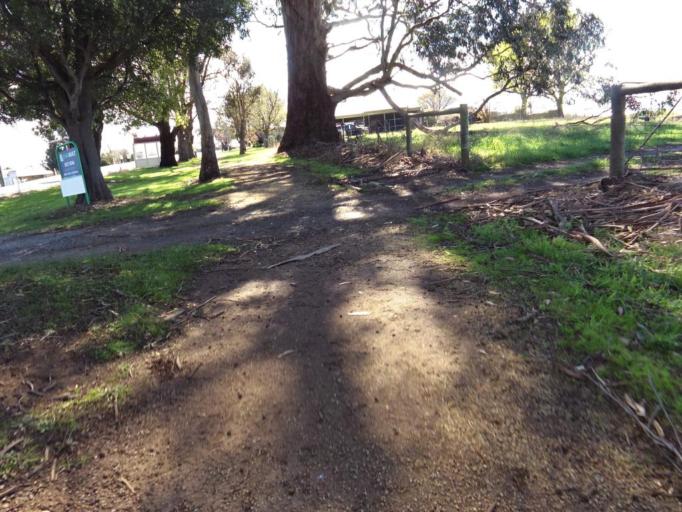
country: AU
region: Victoria
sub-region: Baw Baw
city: Warragul
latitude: -38.0259
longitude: 145.9549
